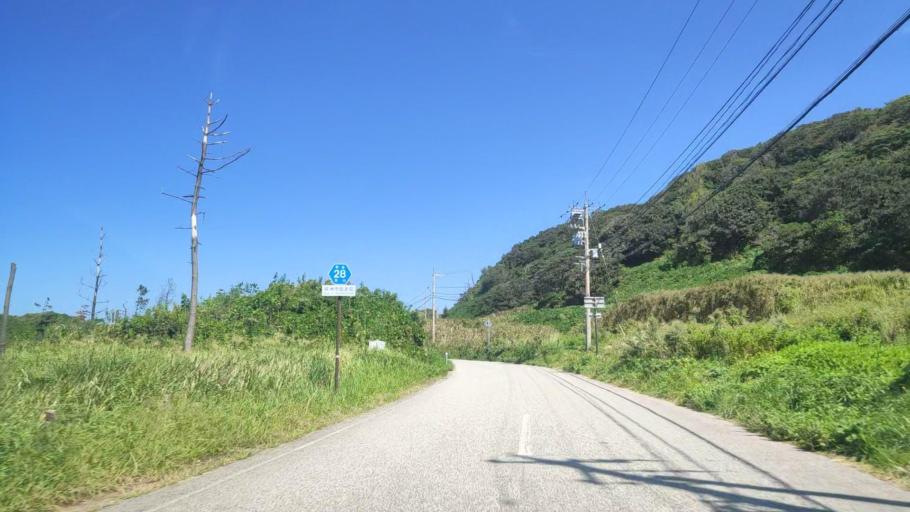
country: JP
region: Ishikawa
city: Nanao
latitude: 37.5147
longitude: 137.2244
